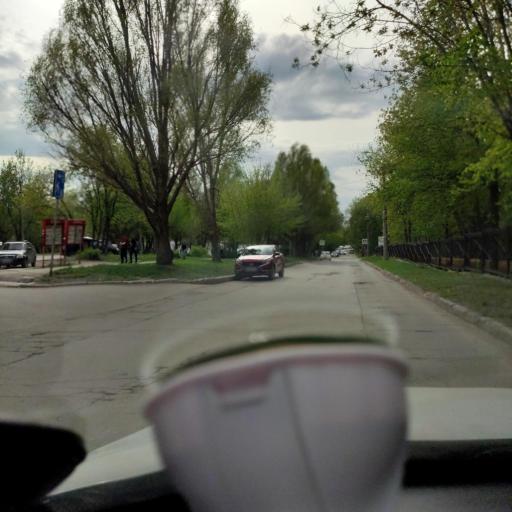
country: RU
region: Samara
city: Novosemeykino
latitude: 53.3433
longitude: 50.2222
